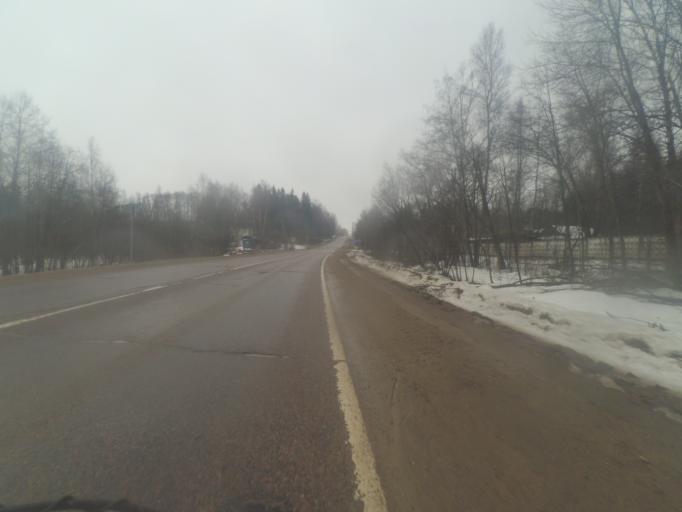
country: RU
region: Moskovskaya
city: Avtopoligon
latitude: 56.2624
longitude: 37.2208
